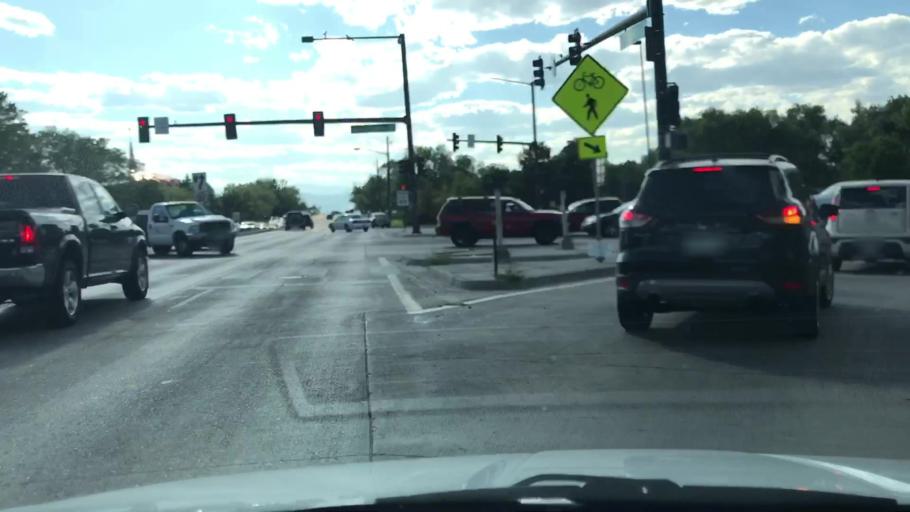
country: US
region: Colorado
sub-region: Arapahoe County
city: Cherry Hills Village
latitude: 39.6531
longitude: -104.9403
